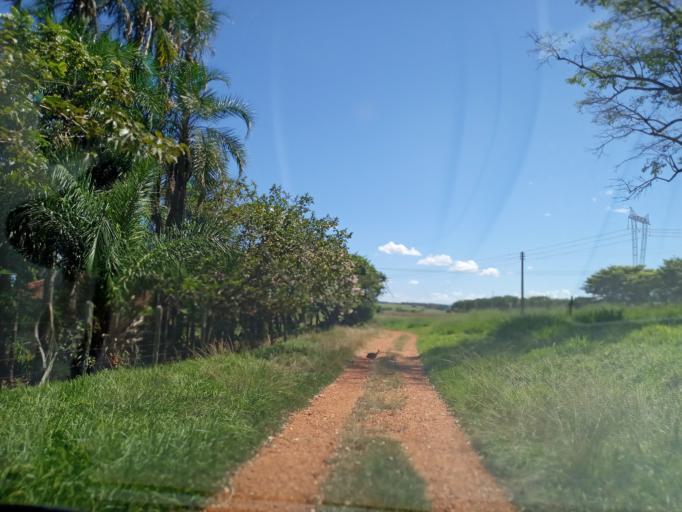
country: BR
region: Goias
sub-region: Itumbiara
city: Itumbiara
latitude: -18.3971
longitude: -49.1259
